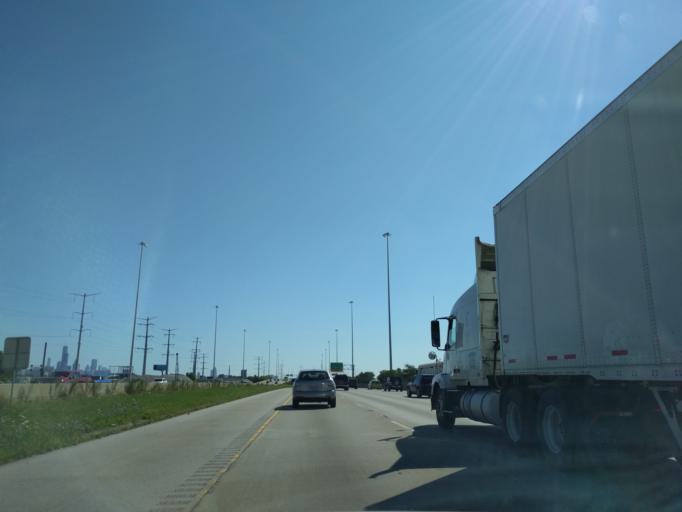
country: US
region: Illinois
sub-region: Cook County
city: Chicago
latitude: 41.8324
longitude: -87.6943
